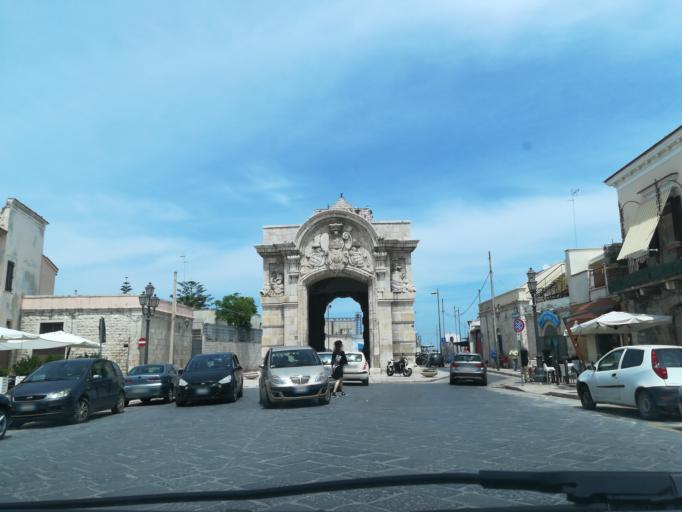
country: IT
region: Apulia
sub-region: Provincia di Barletta - Andria - Trani
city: Barletta
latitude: 41.3224
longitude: 16.2846
